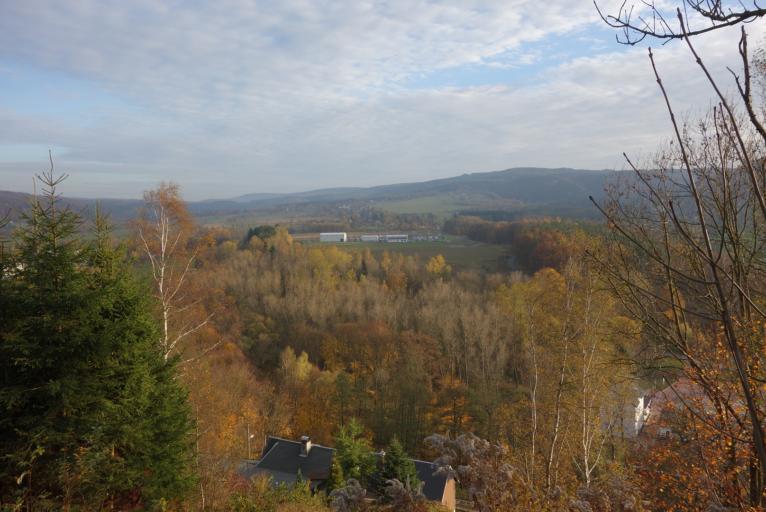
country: DE
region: Saxony
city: Olbernhau
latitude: 50.6519
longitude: 13.3725
